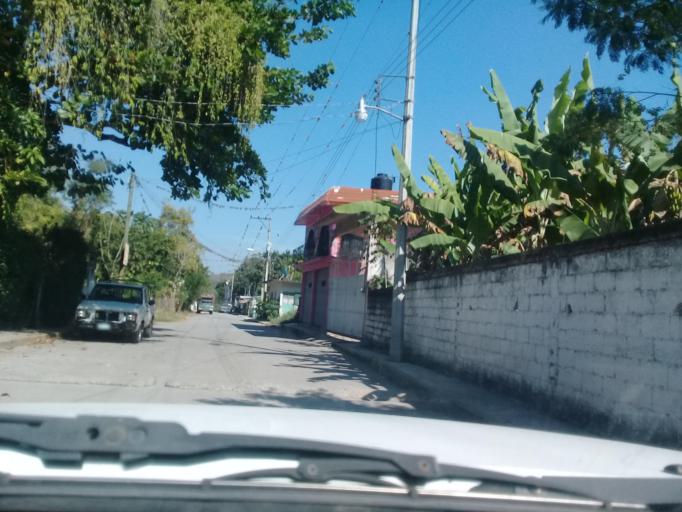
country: MX
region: Veracruz
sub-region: Emiliano Zapata
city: Plan del Rio
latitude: 19.4193
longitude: -96.6152
